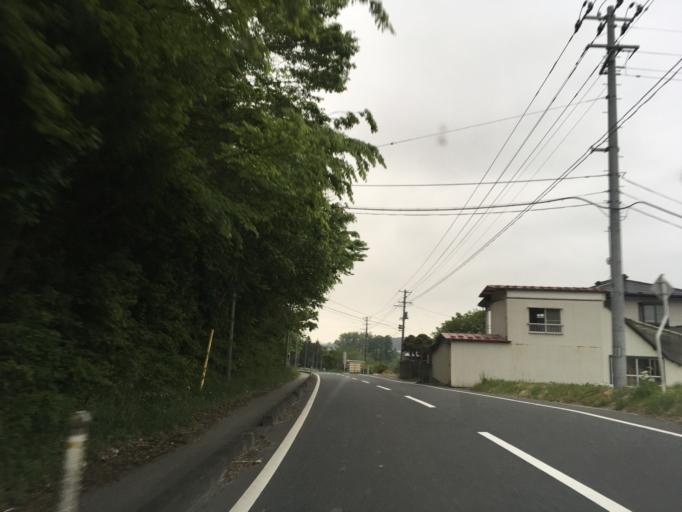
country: JP
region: Iwate
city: Ichinoseki
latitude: 38.7323
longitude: 141.3012
